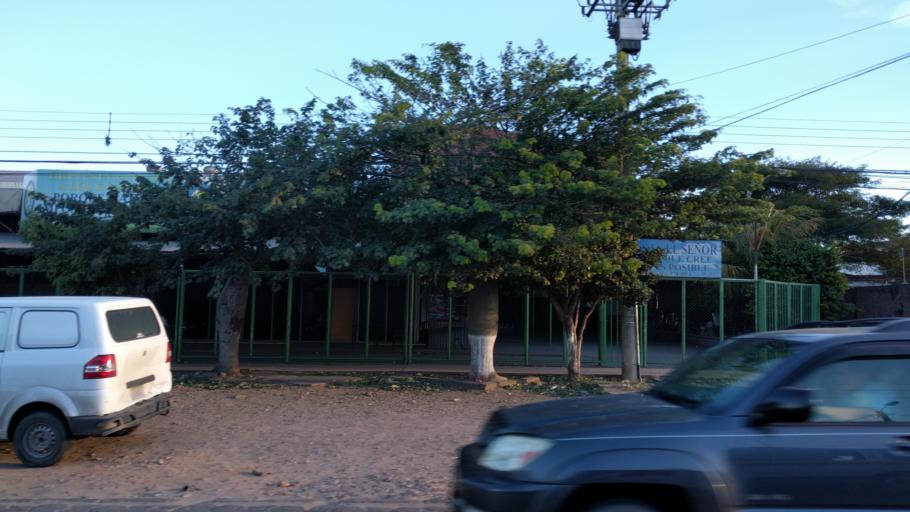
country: BO
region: Santa Cruz
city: Santa Cruz de la Sierra
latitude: -17.7605
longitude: -63.1688
